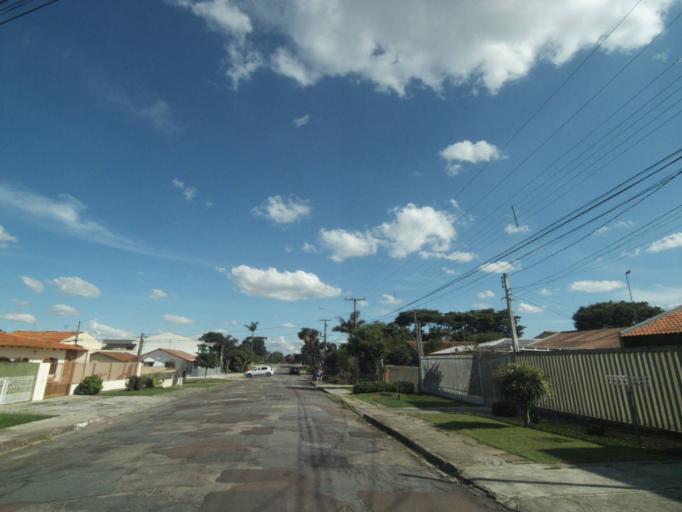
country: BR
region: Parana
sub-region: Pinhais
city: Pinhais
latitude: -25.4523
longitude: -49.2123
